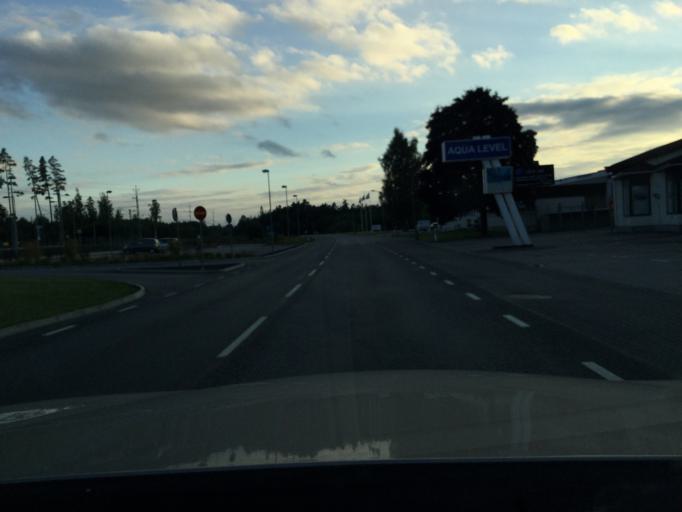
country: SE
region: Kronoberg
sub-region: Almhults Kommun
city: AElmhult
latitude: 56.6340
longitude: 14.2148
